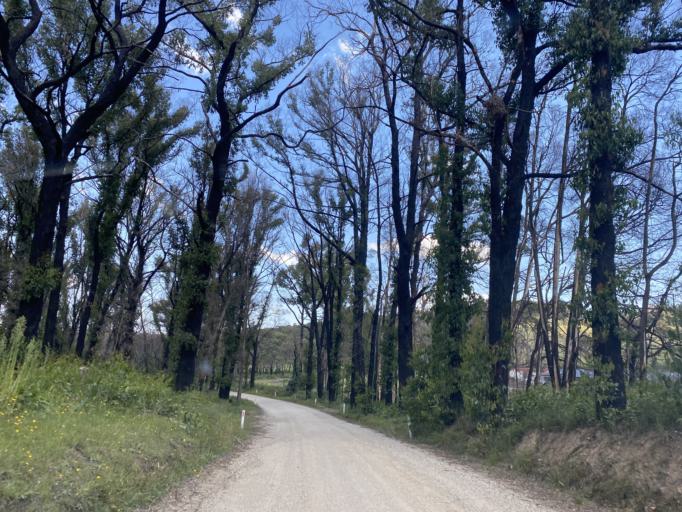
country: AU
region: Victoria
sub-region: Cardinia
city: Garfield
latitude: -38.0029
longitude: 145.7045
